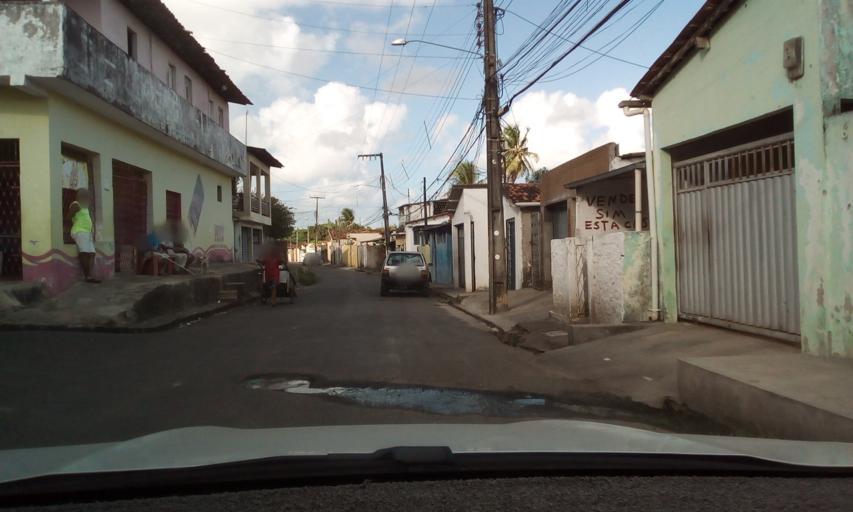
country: BR
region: Paraiba
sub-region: Joao Pessoa
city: Joao Pessoa
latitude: -7.0969
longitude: -34.8612
